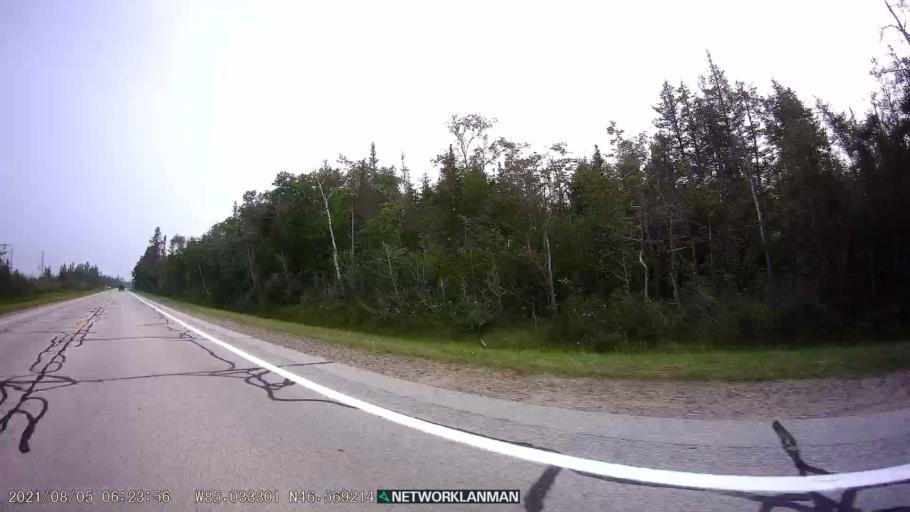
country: US
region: Michigan
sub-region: Luce County
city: Newberry
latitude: 46.5696
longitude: -85.0334
